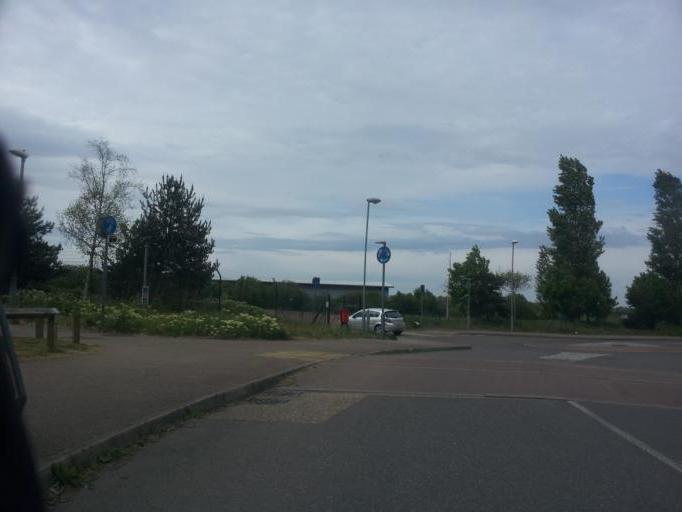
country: GB
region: England
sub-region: Kent
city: Sittingbourne
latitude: 51.3438
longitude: 0.7647
